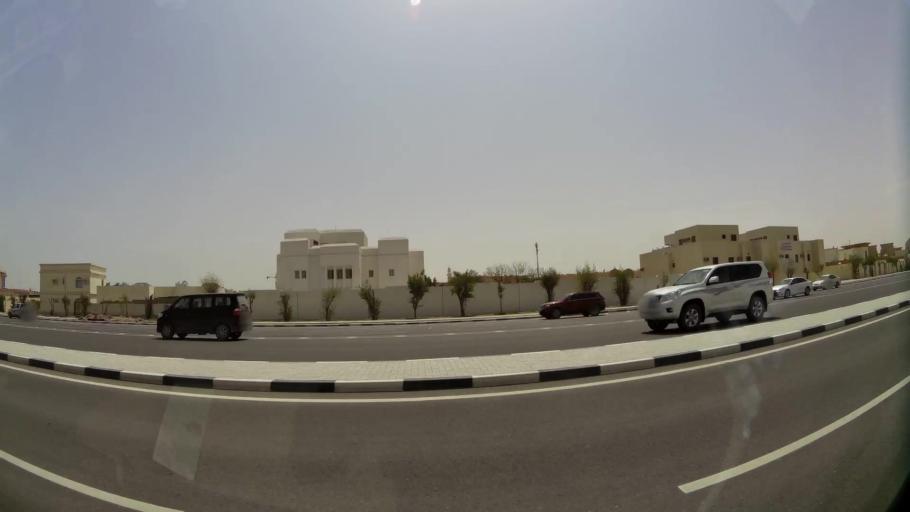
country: QA
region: Baladiyat ar Rayyan
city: Ar Rayyan
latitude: 25.3495
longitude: 51.4761
